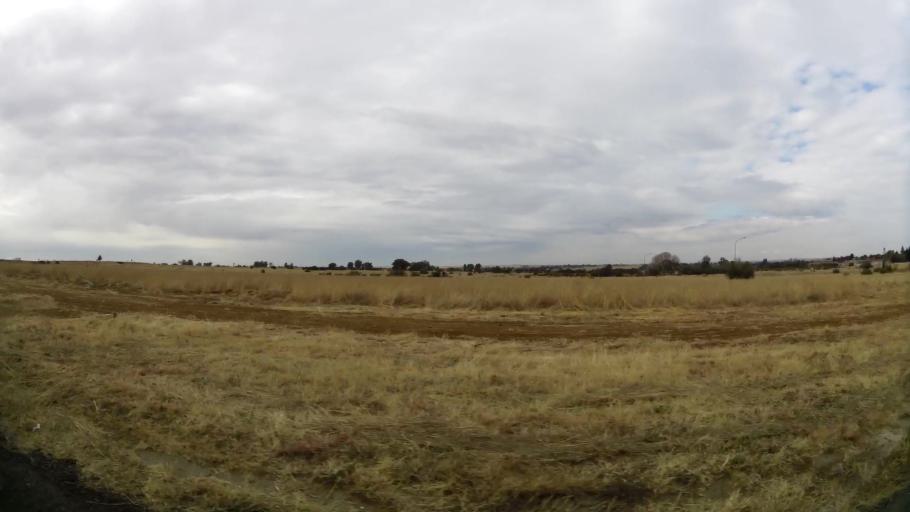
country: ZA
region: Orange Free State
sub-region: Fezile Dabi District Municipality
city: Kroonstad
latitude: -27.6272
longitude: 27.2443
